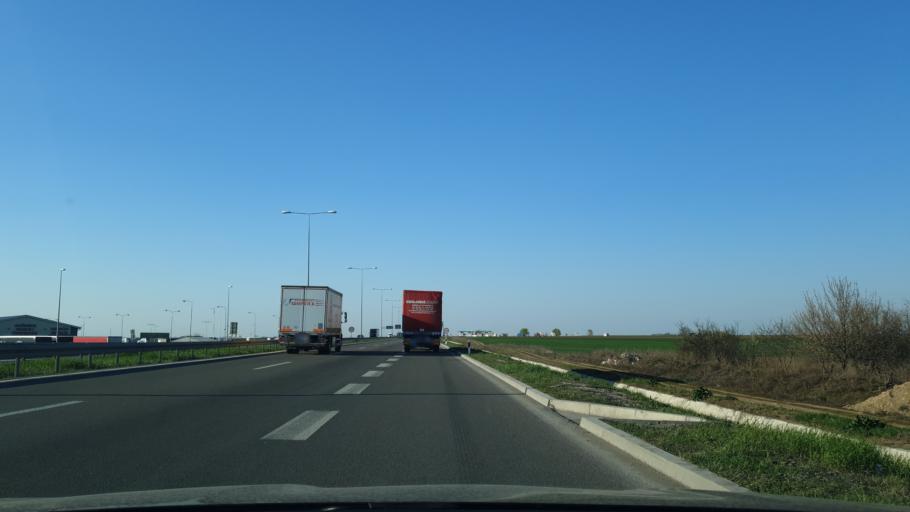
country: RS
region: Central Serbia
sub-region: Belgrade
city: Surcin
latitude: 44.8047
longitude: 20.2545
